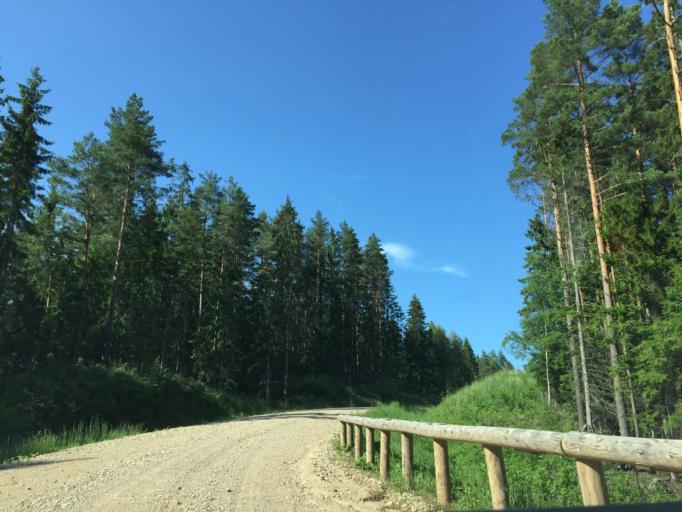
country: LV
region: Tukuma Rajons
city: Tukums
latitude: 57.0153
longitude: 23.2239
